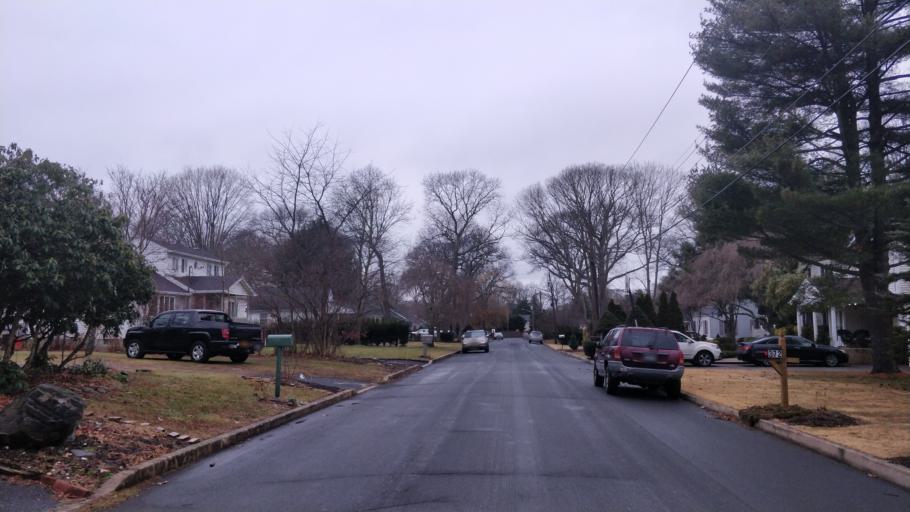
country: US
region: New York
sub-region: Suffolk County
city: Hauppauge
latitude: 40.8310
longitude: -73.2069
